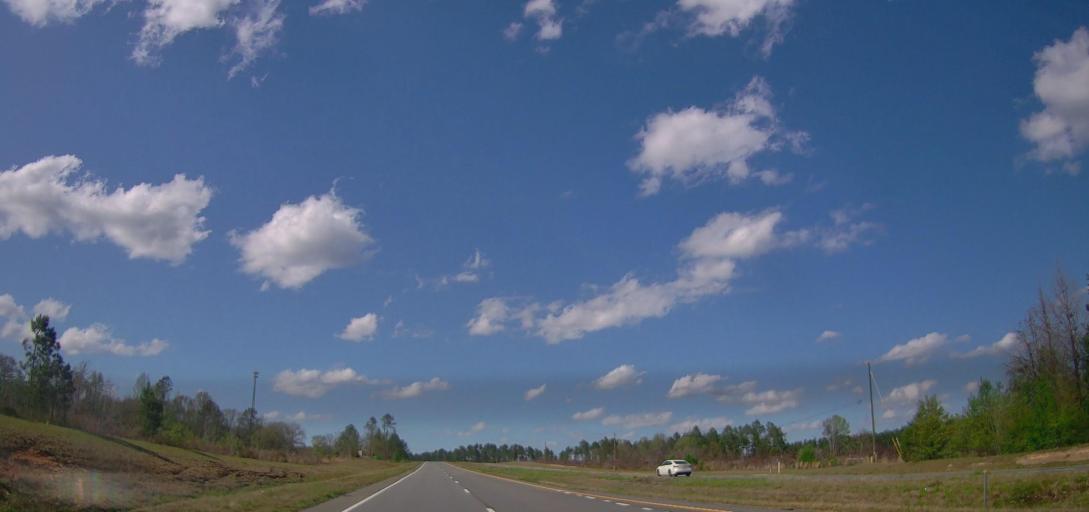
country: US
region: Georgia
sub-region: Baldwin County
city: Hardwick
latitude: 32.9884
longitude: -83.2125
